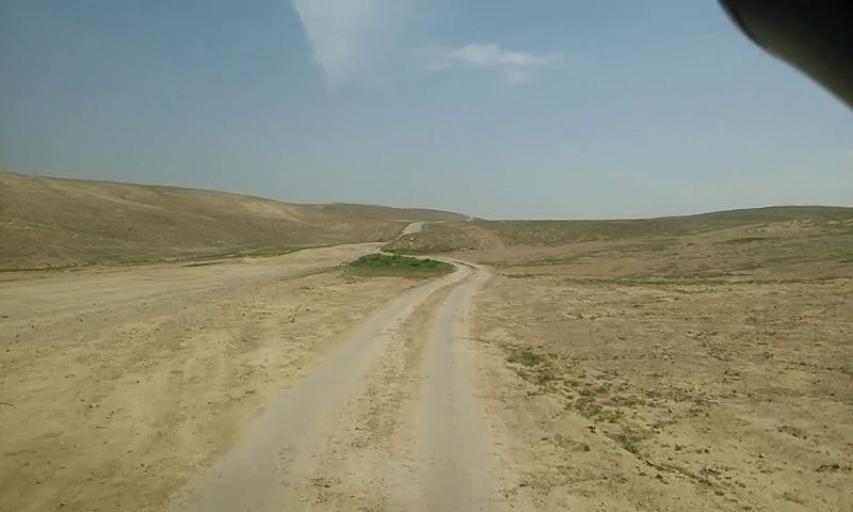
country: PS
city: `Arab ar Rashaydah
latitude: 31.5288
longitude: 35.2906
